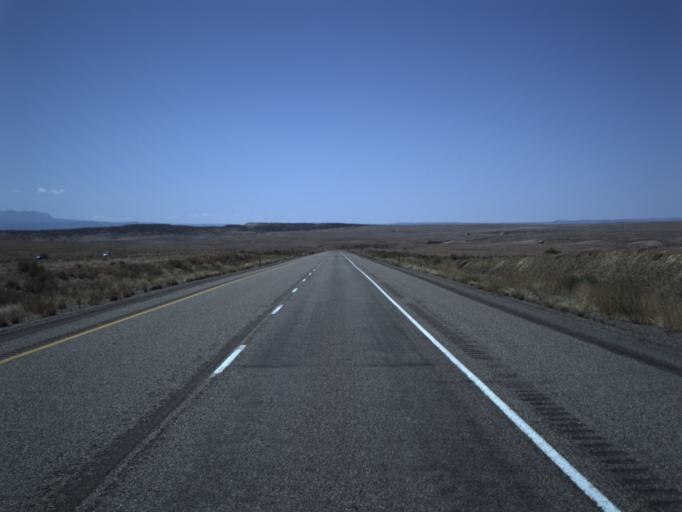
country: US
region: Colorado
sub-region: Mesa County
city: Loma
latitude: 39.1415
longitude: -109.1549
